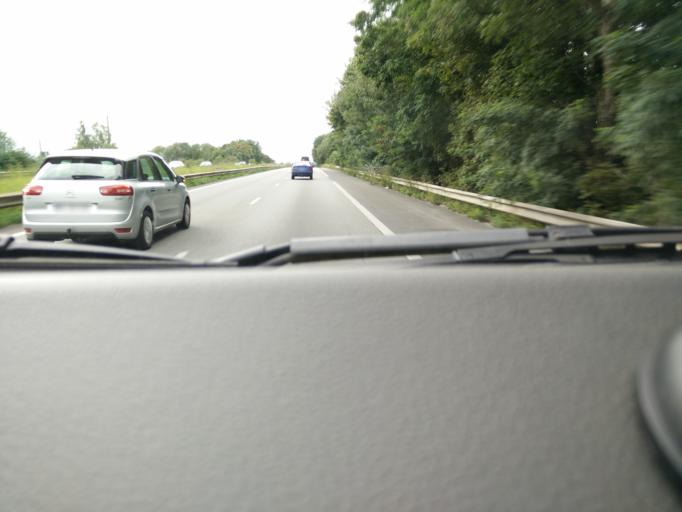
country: FR
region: Nord-Pas-de-Calais
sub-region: Departement du Nord
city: Bouvignies
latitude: 50.4591
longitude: 3.2697
